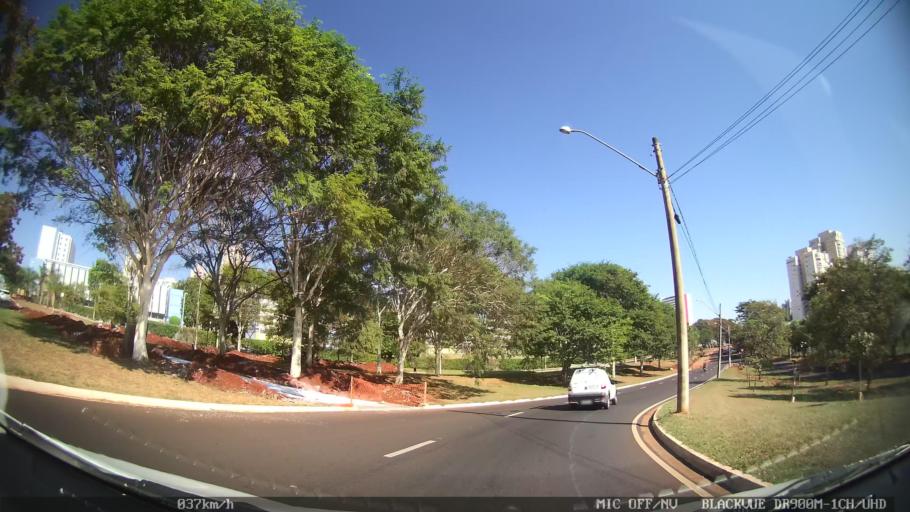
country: BR
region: Sao Paulo
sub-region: Ribeirao Preto
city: Ribeirao Preto
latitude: -21.2176
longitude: -47.8159
